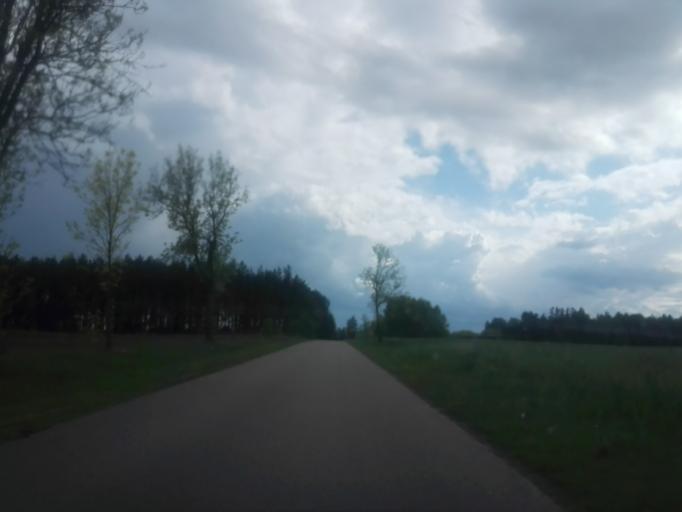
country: PL
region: Podlasie
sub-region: Powiat lomzynski
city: Wizna
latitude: 53.2666
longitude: 22.4509
